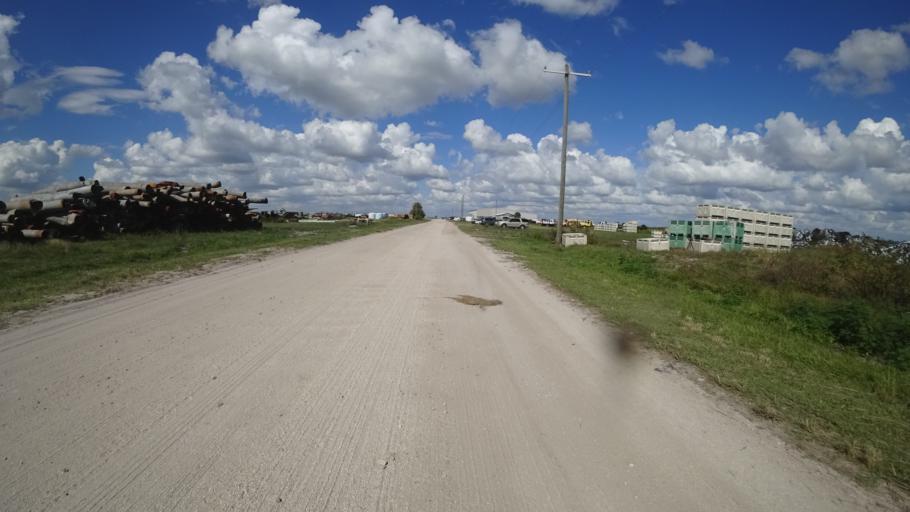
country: US
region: Florida
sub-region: DeSoto County
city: Arcadia
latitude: 27.3152
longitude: -82.1007
